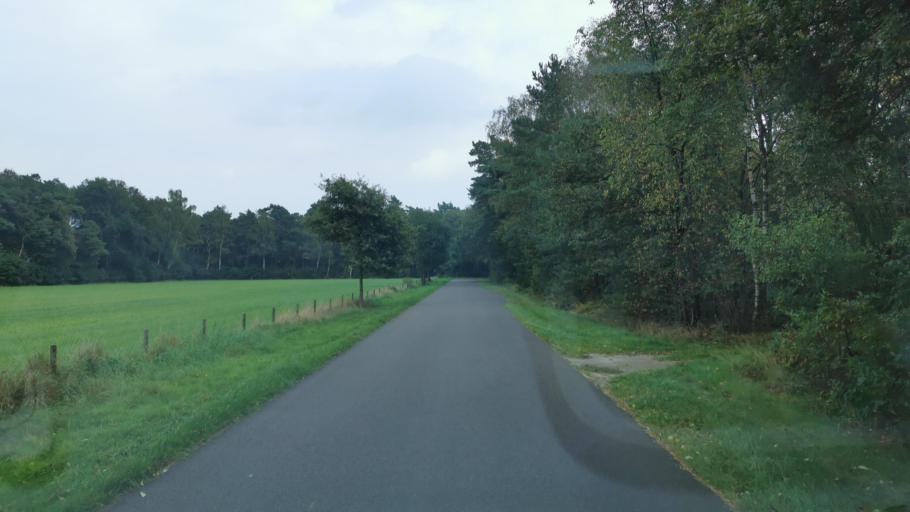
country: NL
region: Overijssel
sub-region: Gemeente Losser
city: Losser
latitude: 52.3136
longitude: 7.0365
